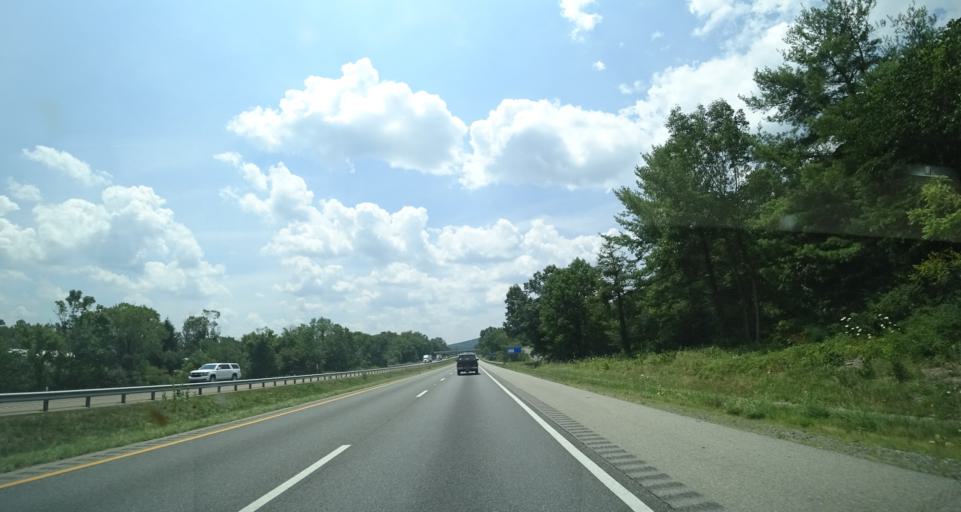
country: US
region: Virginia
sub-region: Pulaski County
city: Pulaski
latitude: 36.9842
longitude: -80.8255
